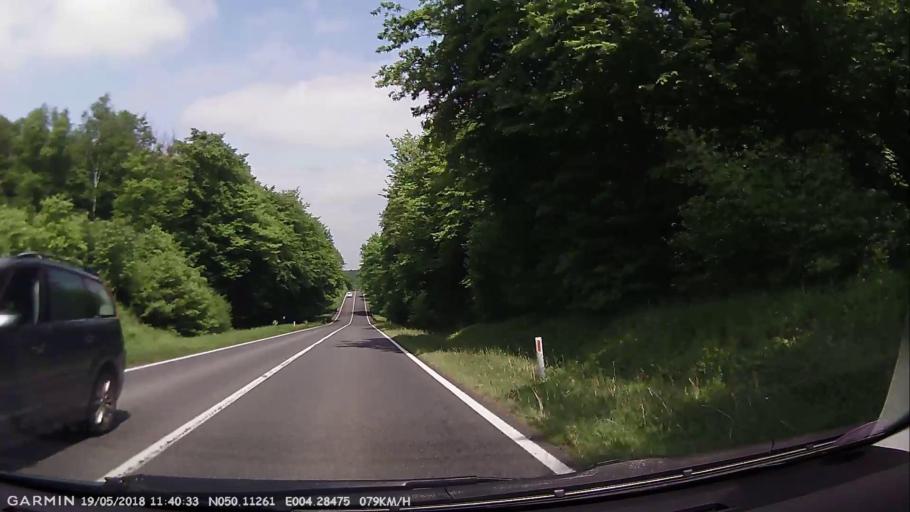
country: BE
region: Wallonia
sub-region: Province du Hainaut
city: Froidchapelle
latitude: 50.1128
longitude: 4.2847
